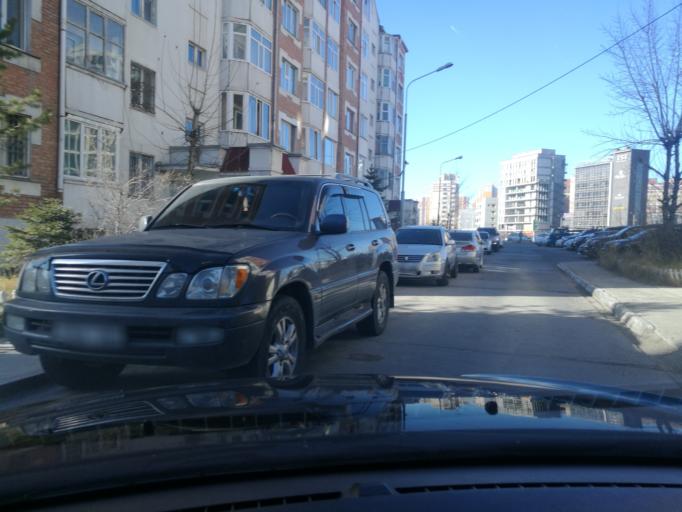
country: MN
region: Ulaanbaatar
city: Ulaanbaatar
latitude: 47.9051
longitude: 106.9094
